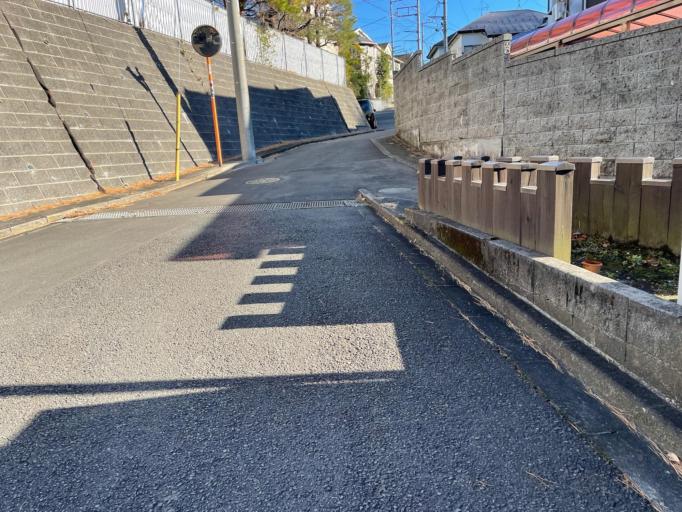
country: JP
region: Tokyo
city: Chofugaoka
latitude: 35.6299
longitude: 139.5222
